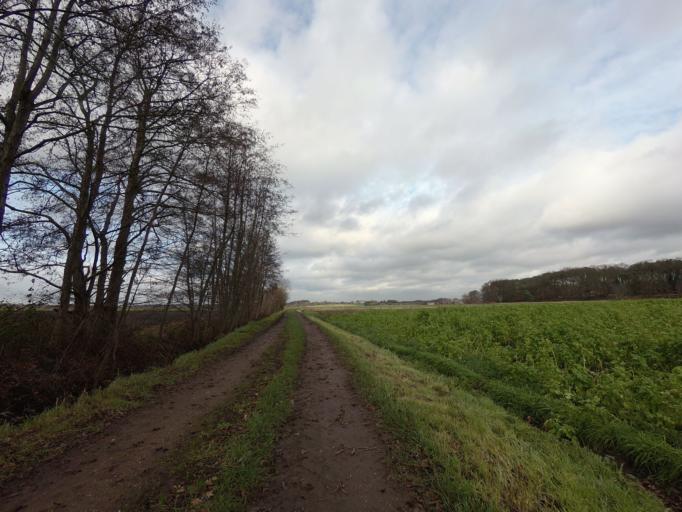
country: BE
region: Flanders
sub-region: Provincie Antwerpen
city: Stabroek
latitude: 51.3739
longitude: 4.3292
